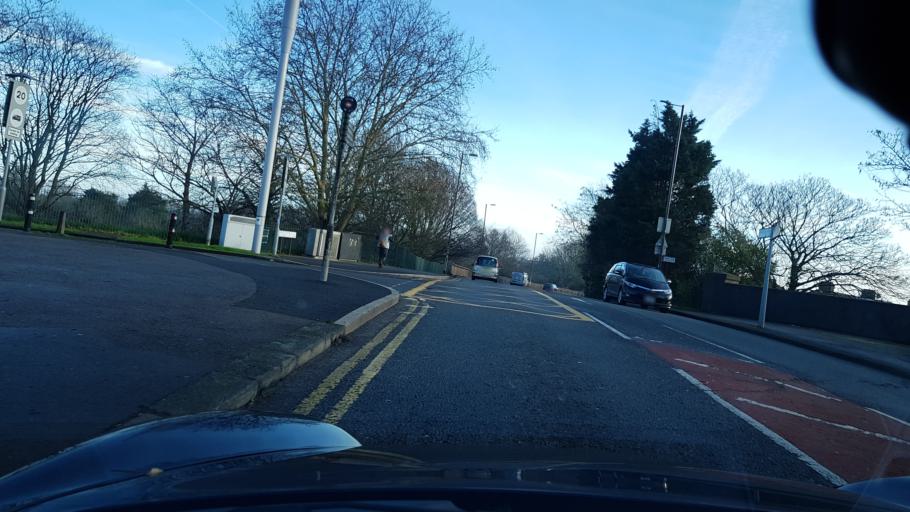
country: GB
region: England
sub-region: Greater London
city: Morden
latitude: 51.4028
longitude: -0.2050
